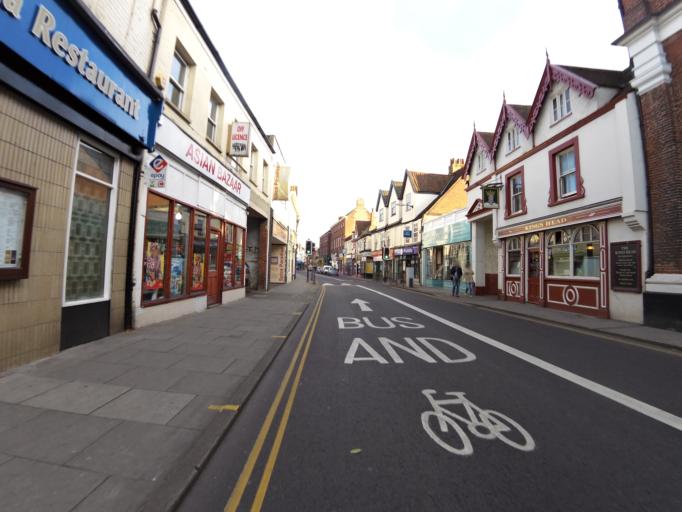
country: GB
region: England
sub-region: Norfolk
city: Norwich
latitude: 52.6350
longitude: 1.2966
